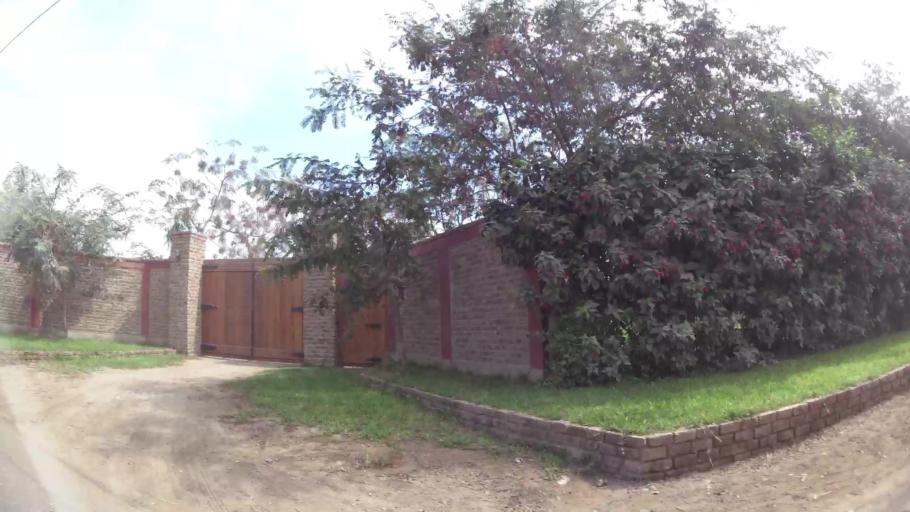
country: PE
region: Lima
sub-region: Provincia de Canete
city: Mala
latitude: -12.7301
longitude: -76.6209
